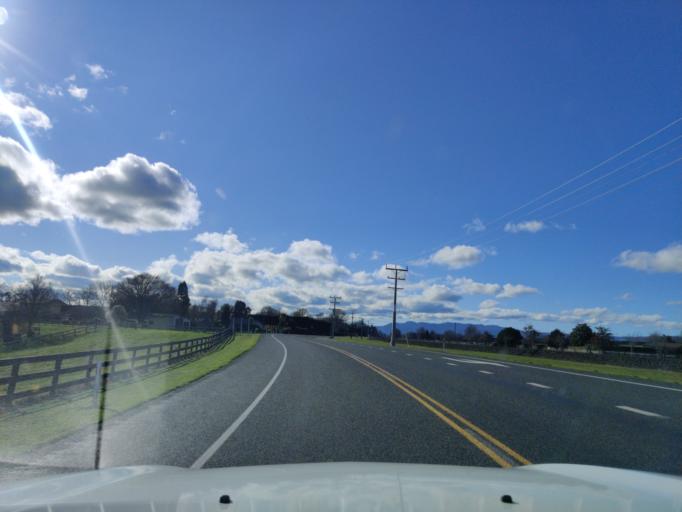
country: NZ
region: Waikato
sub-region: Matamata-Piako District
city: Matamata
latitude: -37.8631
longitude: 175.7542
